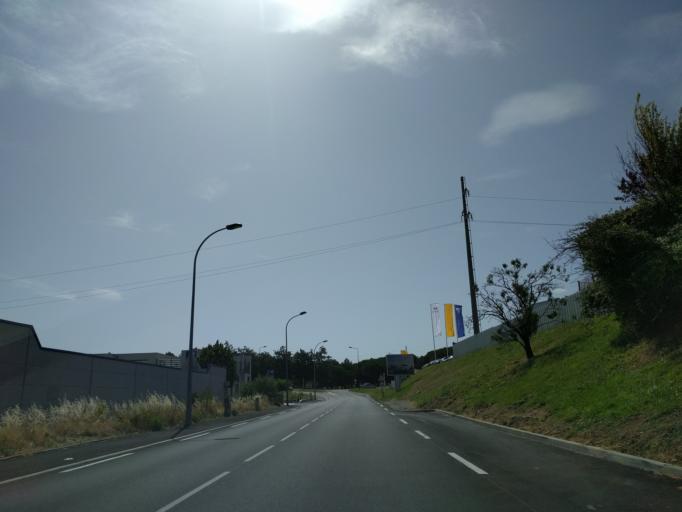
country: FR
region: Languedoc-Roussillon
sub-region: Departement de l'Aude
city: Palaja
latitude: 43.2081
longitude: 2.3859
